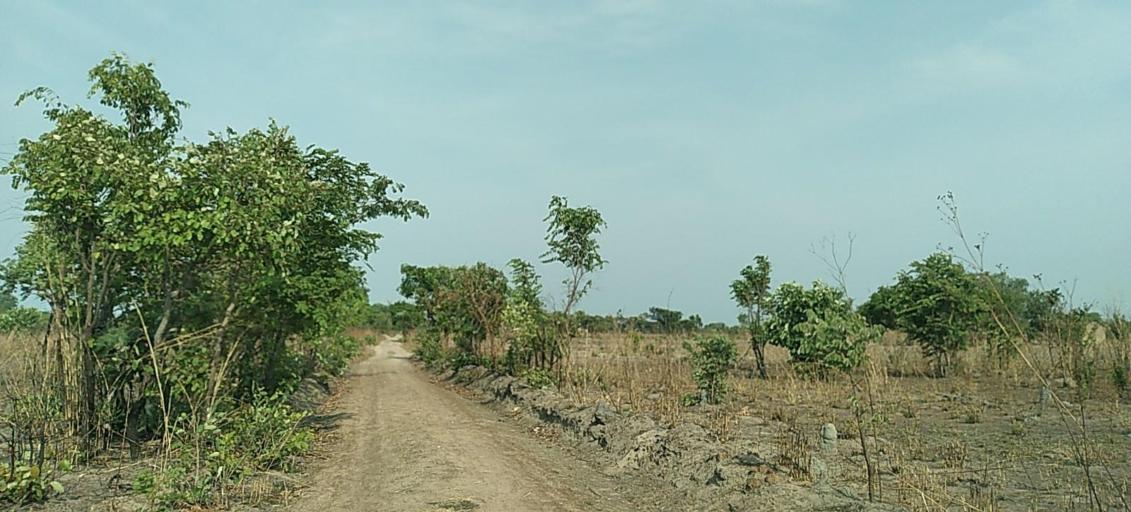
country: ZM
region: Copperbelt
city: Luanshya
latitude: -13.2170
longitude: 28.6482
